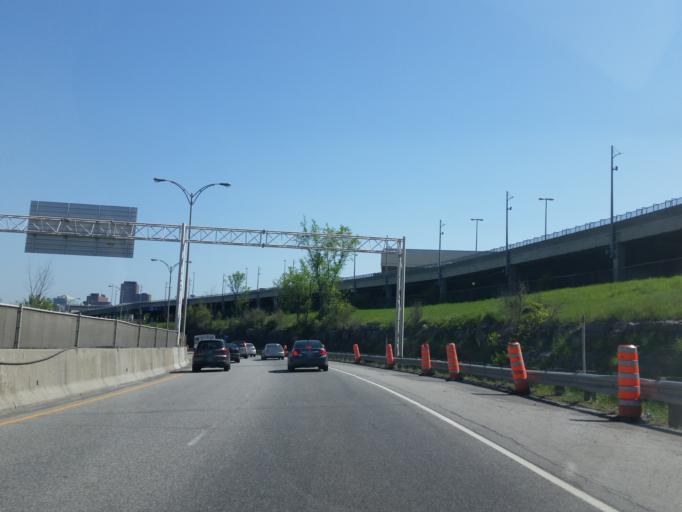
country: CA
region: Quebec
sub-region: Outaouais
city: Gatineau
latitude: 45.4437
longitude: -75.7315
